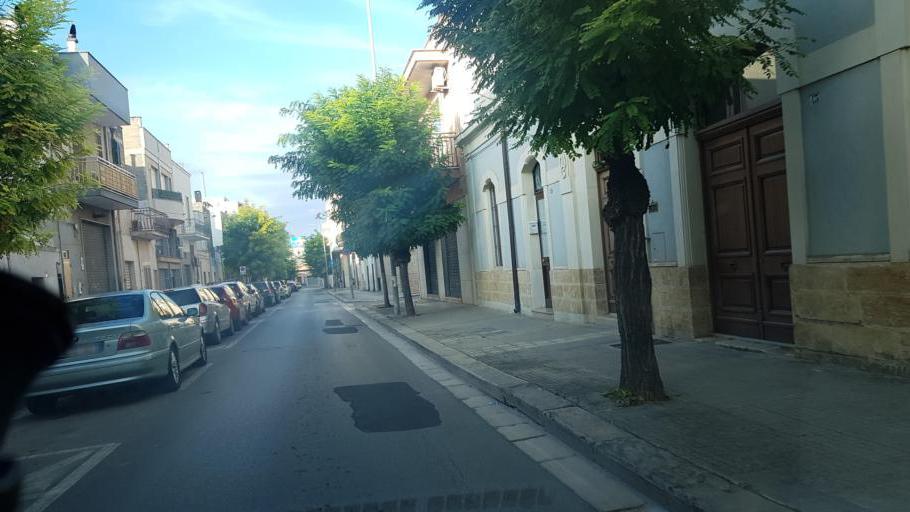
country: IT
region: Apulia
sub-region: Provincia di Brindisi
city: Francavilla Fontana
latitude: 40.5306
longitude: 17.5865
